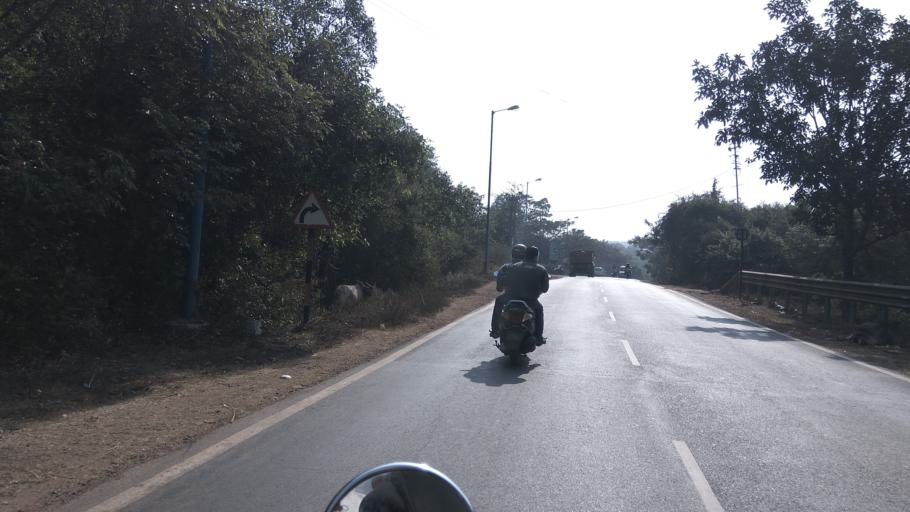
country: IN
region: Goa
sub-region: North Goa
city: Bandora
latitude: 15.4488
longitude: 73.9710
